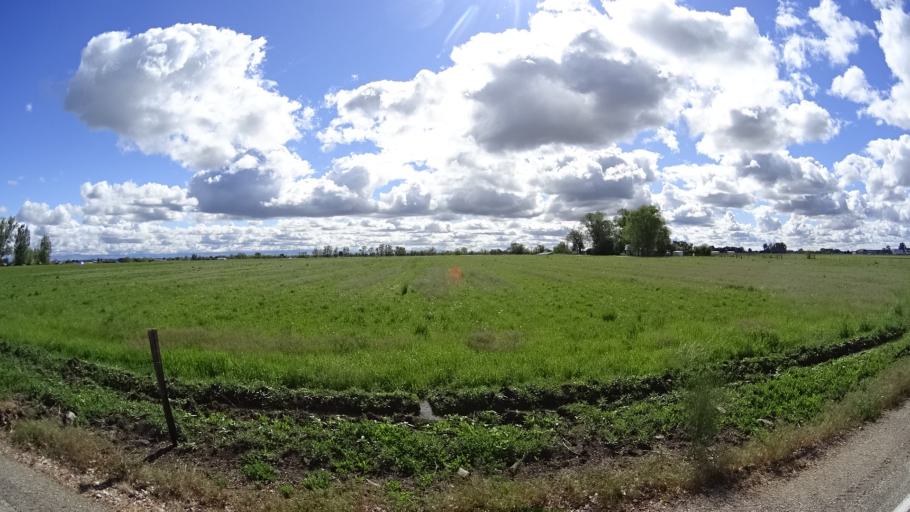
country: US
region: Idaho
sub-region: Ada County
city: Kuna
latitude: 43.5109
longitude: -116.4740
